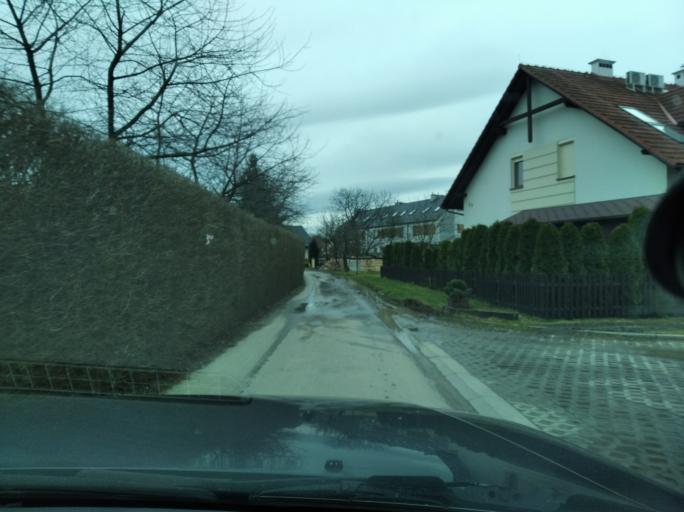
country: PL
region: Subcarpathian Voivodeship
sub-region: Rzeszow
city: Rzeszow
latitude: 49.9992
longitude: 21.9886
